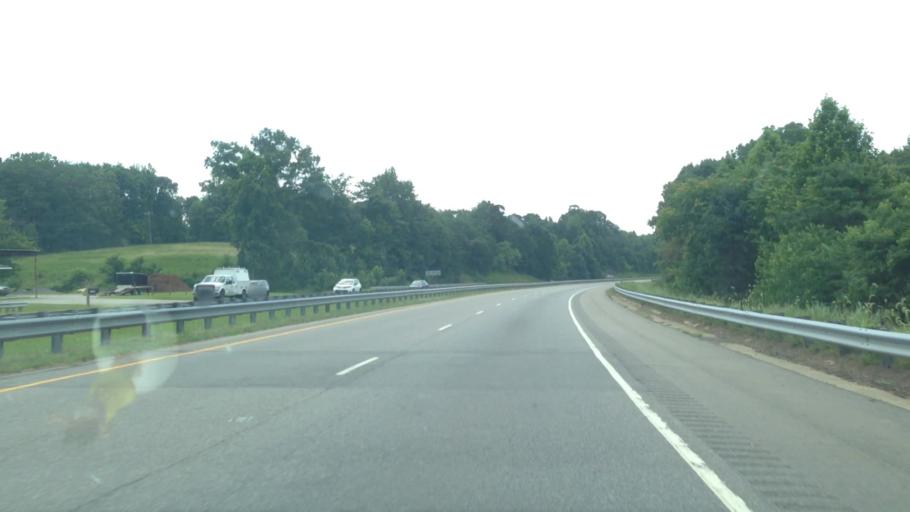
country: US
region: North Carolina
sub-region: Rockingham County
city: Stoneville
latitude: 36.5166
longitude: -79.9173
